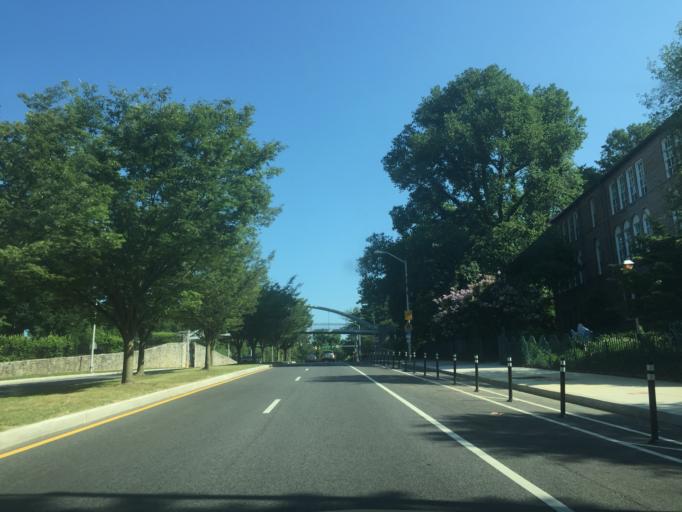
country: US
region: Maryland
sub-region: Baltimore County
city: Towson
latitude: 39.3572
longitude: -76.6348
